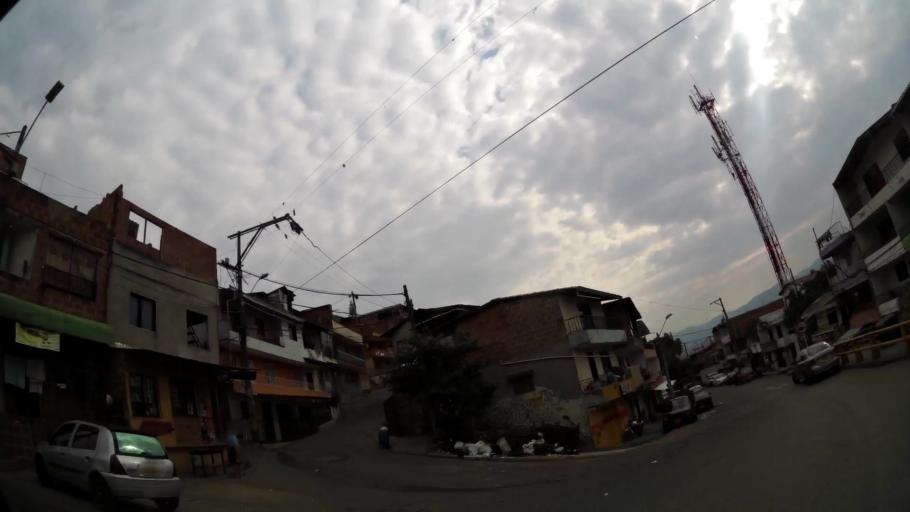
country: CO
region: Antioquia
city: Bello
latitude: 6.3055
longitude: -75.5517
